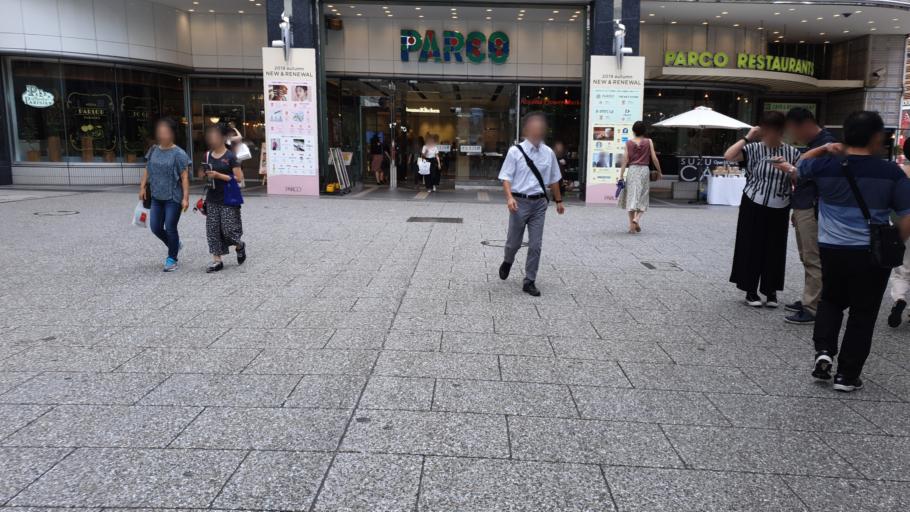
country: JP
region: Hiroshima
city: Hiroshima-shi
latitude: 34.3926
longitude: 132.4618
